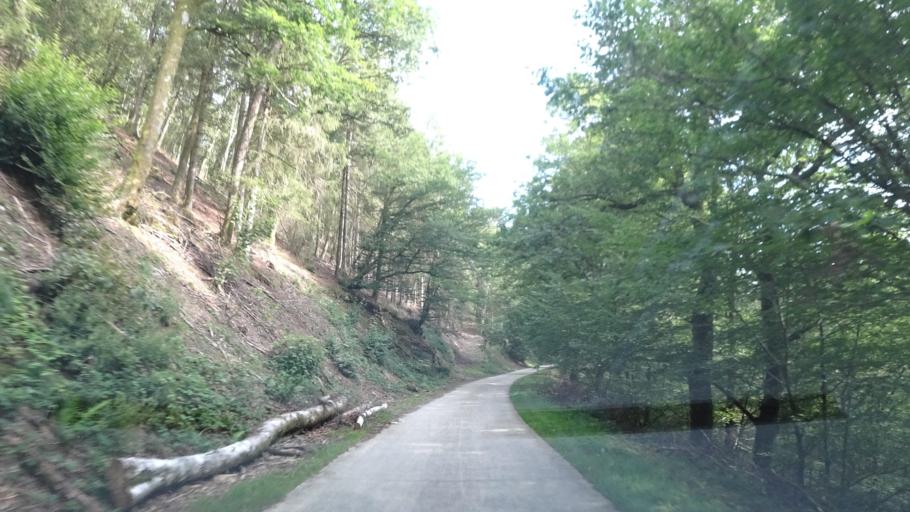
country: BE
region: Wallonia
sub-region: Province du Luxembourg
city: Herbeumont
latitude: 49.7715
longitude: 5.2492
